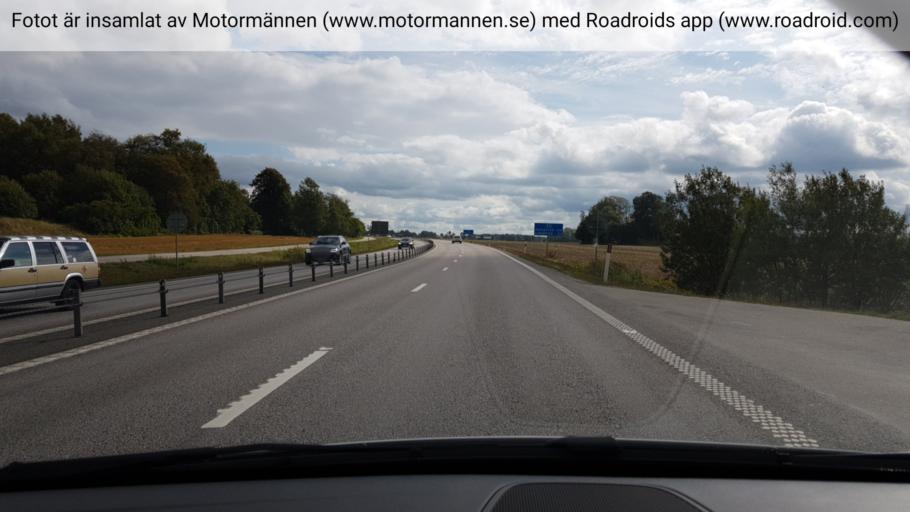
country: SE
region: Vaestra Goetaland
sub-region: Vanersborgs Kommun
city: Vargon
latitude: 58.2896
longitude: 12.3969
